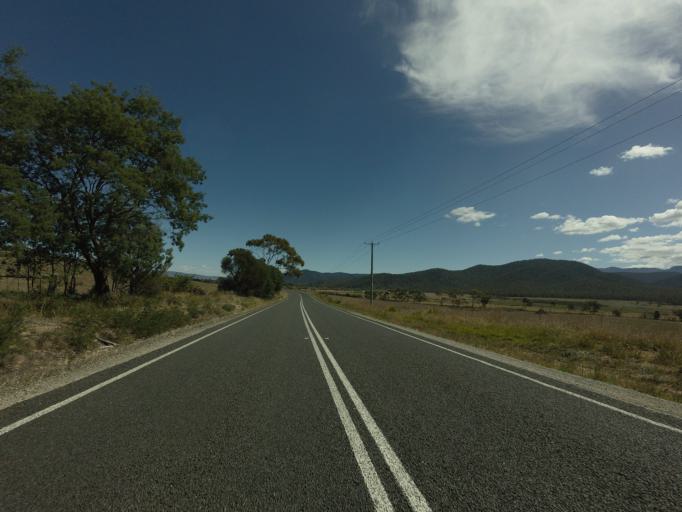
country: AU
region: Tasmania
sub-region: Break O'Day
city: St Helens
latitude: -41.6936
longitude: 147.8665
